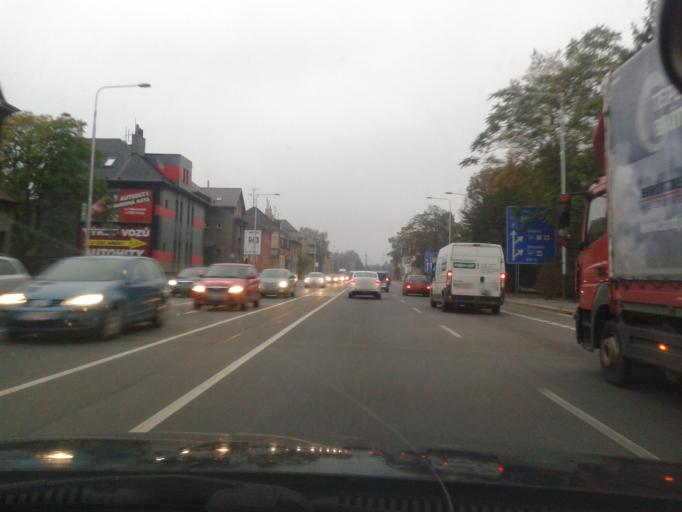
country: CZ
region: Moravskoslezsky
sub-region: Okres Ostrava-Mesto
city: Ostrava
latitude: 49.8006
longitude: 18.2541
